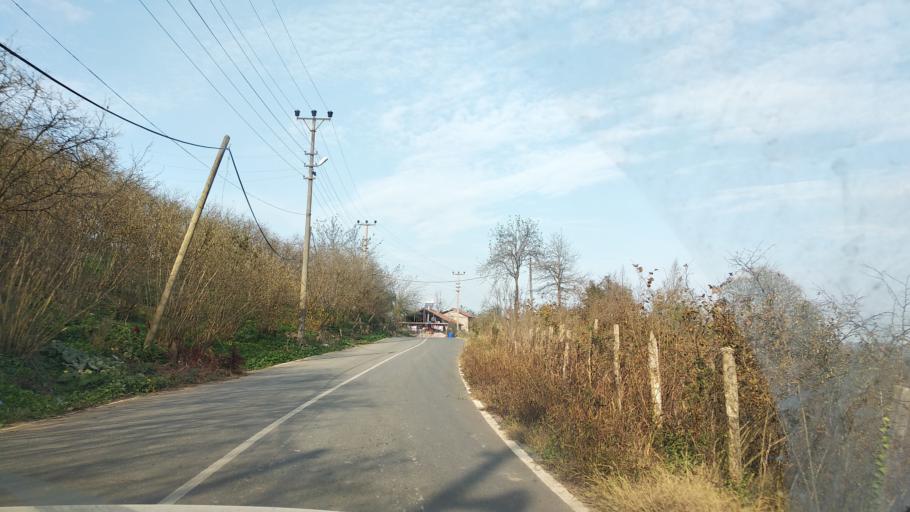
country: TR
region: Sakarya
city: Karasu
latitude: 41.0786
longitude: 30.6075
